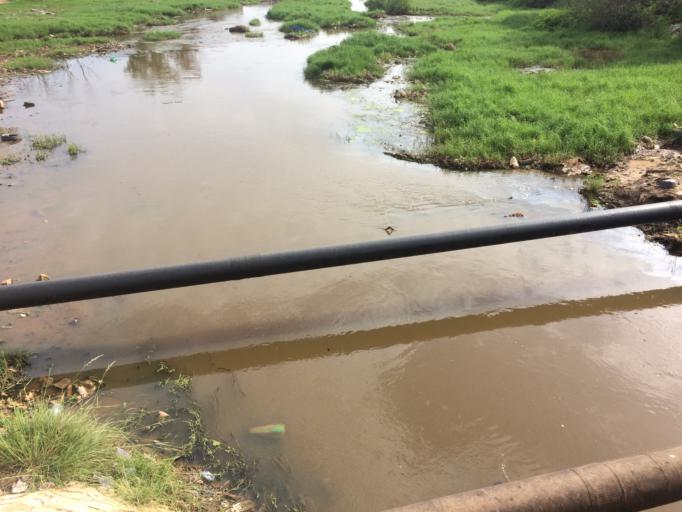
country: SN
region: Dakar
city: Pikine
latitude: 14.7472
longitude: -17.3236
